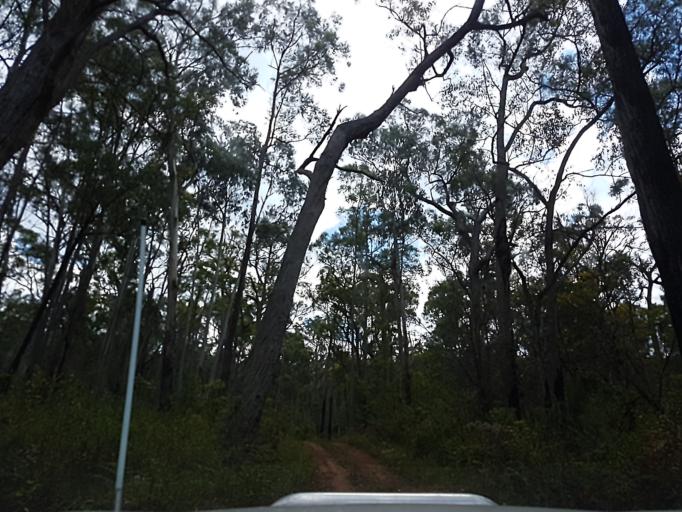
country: AU
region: Victoria
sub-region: East Gippsland
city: Lakes Entrance
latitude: -37.3530
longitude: 148.3565
